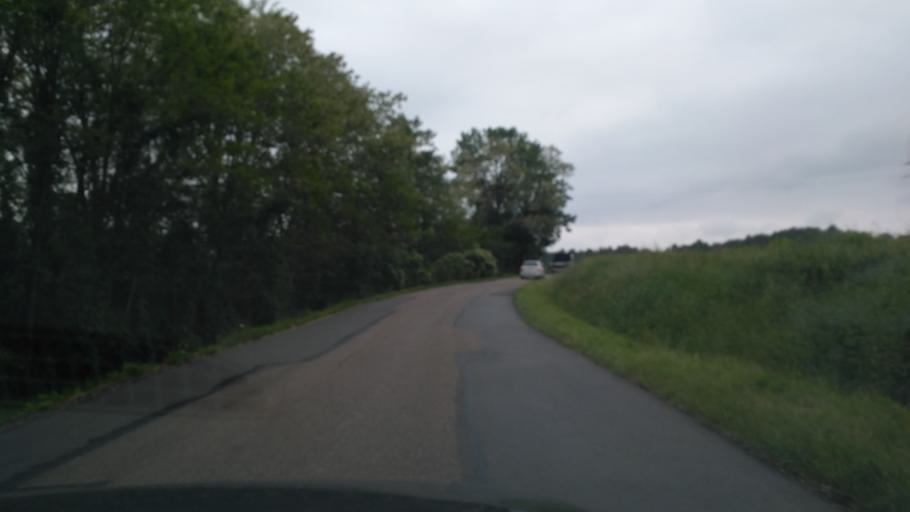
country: PL
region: Subcarpathian Voivodeship
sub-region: Powiat kolbuszowski
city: Niwiska
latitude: 50.1609
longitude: 21.6675
